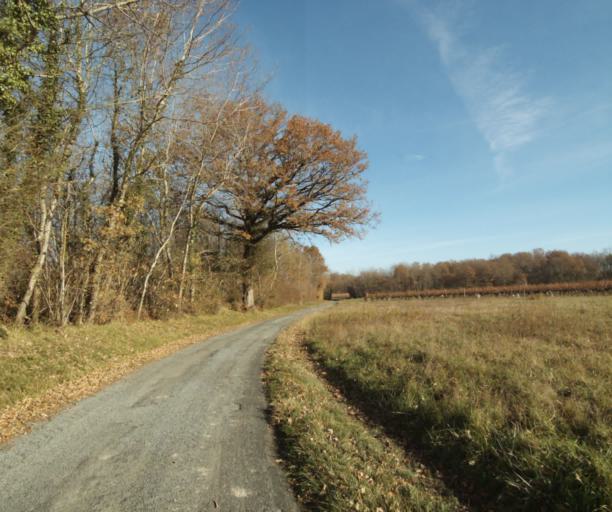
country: FR
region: Poitou-Charentes
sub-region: Departement de la Charente-Maritime
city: Ecoyeux
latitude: 45.7532
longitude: -0.4920
